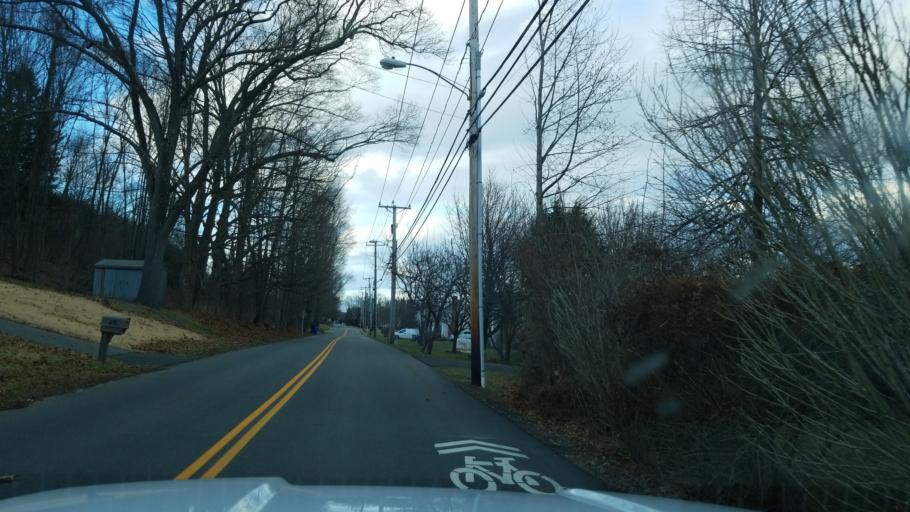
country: US
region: Connecticut
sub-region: Middlesex County
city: Middletown
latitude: 41.5198
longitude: -72.6334
